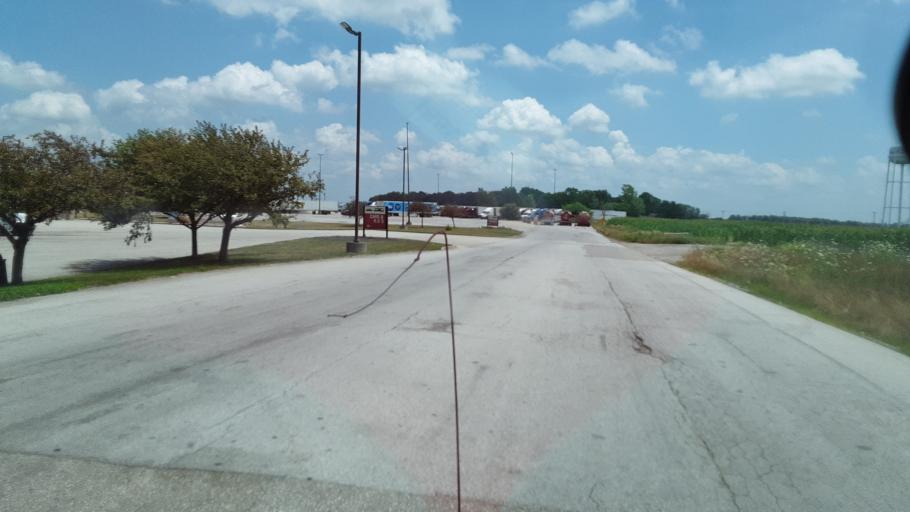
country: US
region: Indiana
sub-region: Henry County
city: New Castle
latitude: 39.8514
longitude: -85.4145
